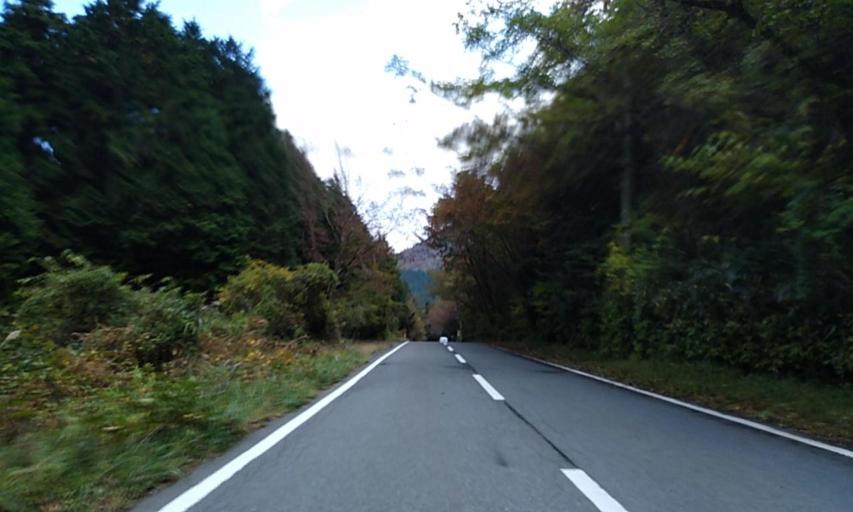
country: JP
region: Shizuoka
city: Gotemba
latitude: 35.2629
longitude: 138.8088
